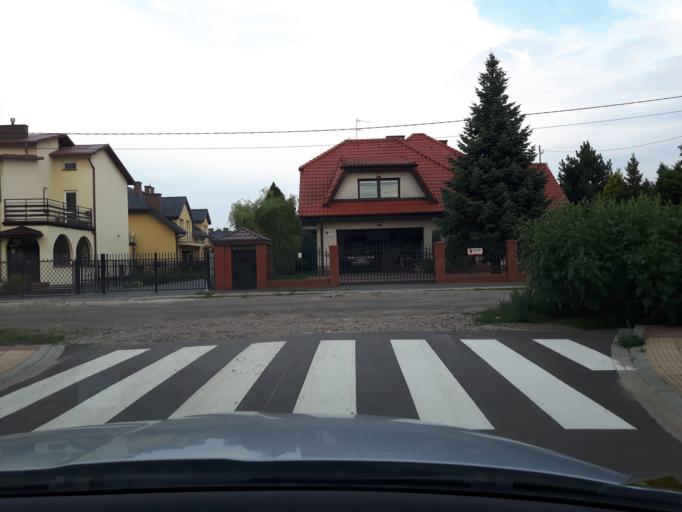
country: PL
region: Masovian Voivodeship
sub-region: Powiat wolominski
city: Zabki
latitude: 52.3040
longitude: 21.0994
